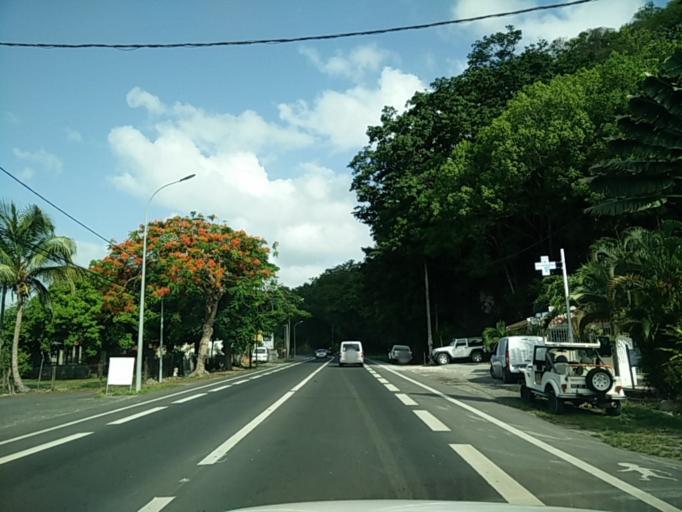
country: GP
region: Guadeloupe
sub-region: Guadeloupe
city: Le Gosier
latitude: 16.2187
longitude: -61.5015
